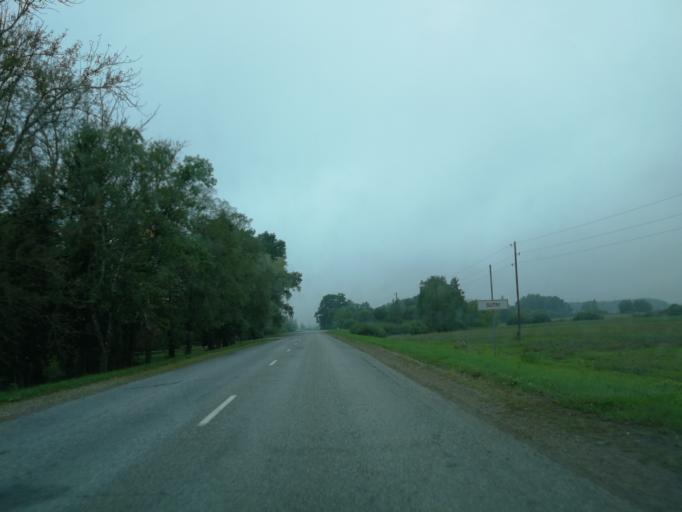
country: LV
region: Varkava
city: Vecvarkava
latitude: 56.3123
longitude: 26.5403
